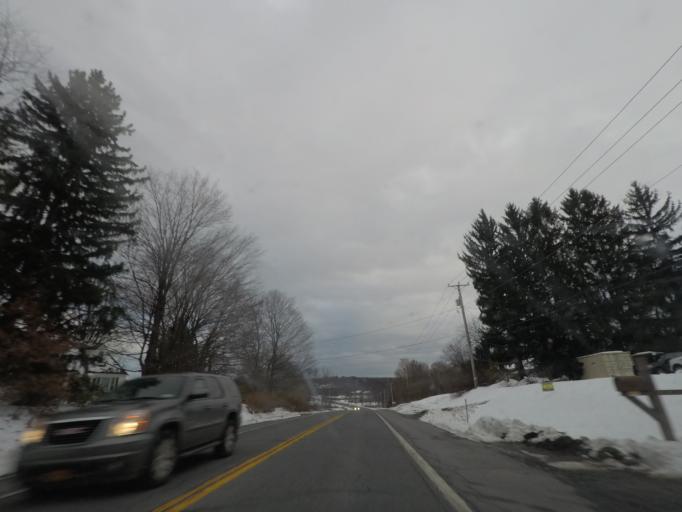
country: US
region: New York
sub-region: Ulster County
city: Plattekill
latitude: 41.6442
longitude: -74.1119
